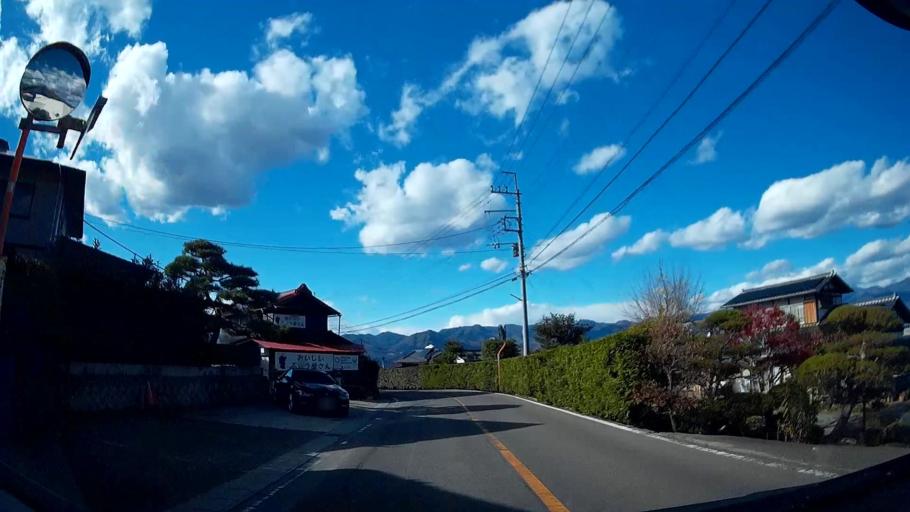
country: JP
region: Yamanashi
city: Enzan
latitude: 35.6495
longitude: 138.7181
